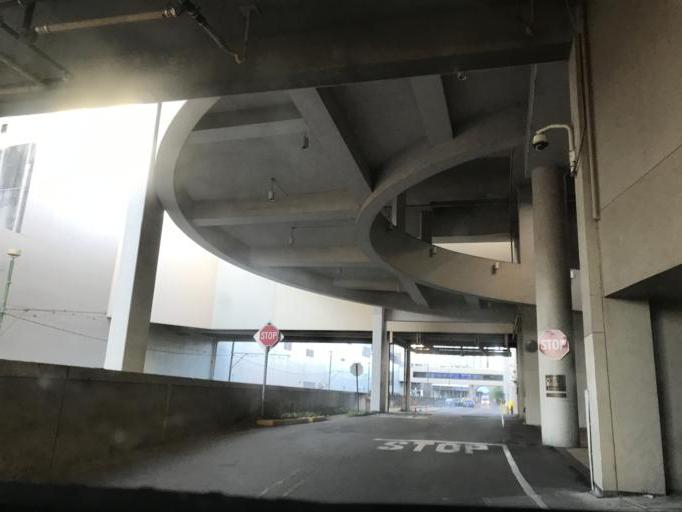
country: US
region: Louisiana
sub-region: Orleans Parish
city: New Orleans
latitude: 29.9461
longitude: -90.0627
